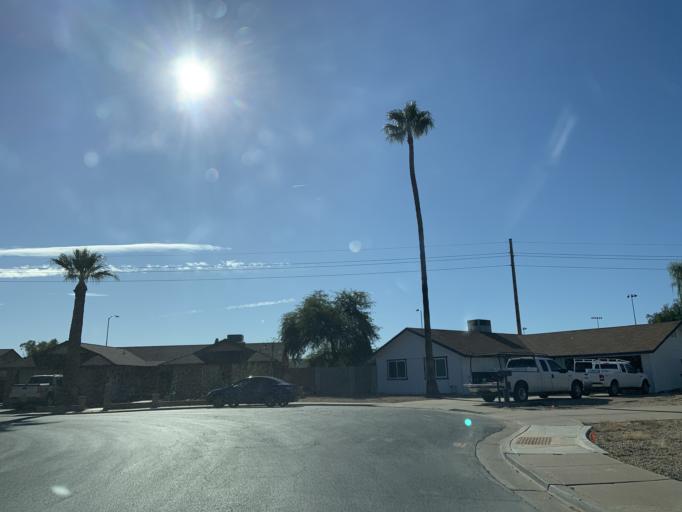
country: US
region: Arizona
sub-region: Maricopa County
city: San Carlos
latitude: 33.3649
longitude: -111.8697
